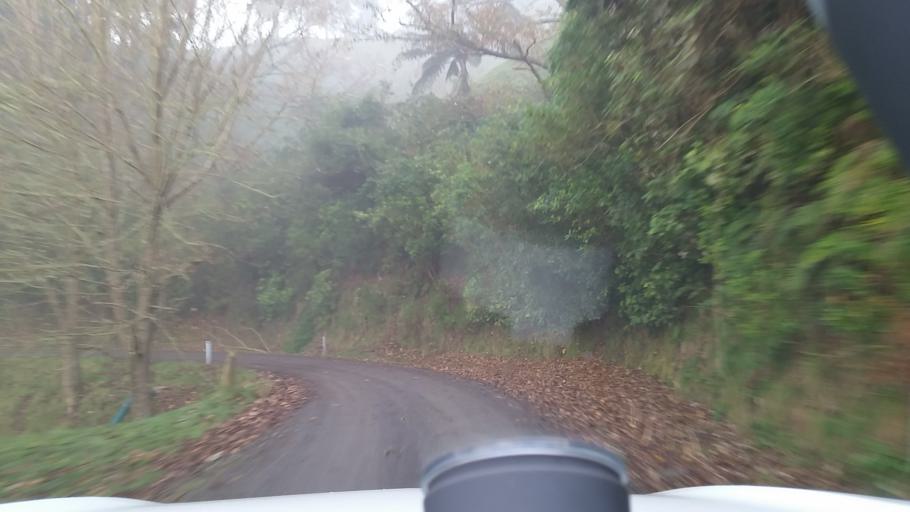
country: NZ
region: Taranaki
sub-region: South Taranaki District
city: Eltham
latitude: -39.4360
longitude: 174.4492
